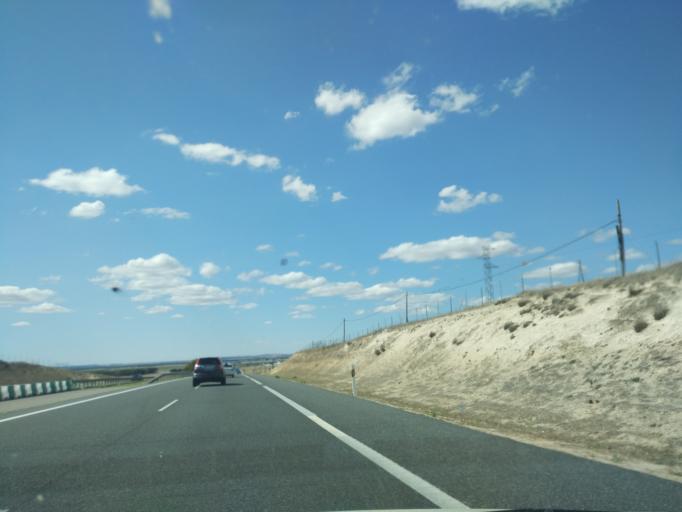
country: ES
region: Castille and Leon
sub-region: Provincia de Valladolid
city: San Vicente del Palacio
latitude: 41.2070
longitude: -4.8289
